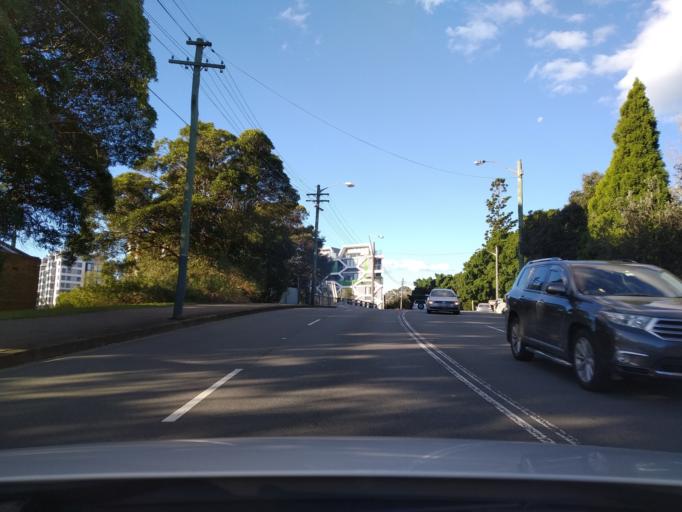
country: AU
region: New South Wales
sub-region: Ashfield
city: Summer Hill
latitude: -33.8954
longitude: 151.1420
